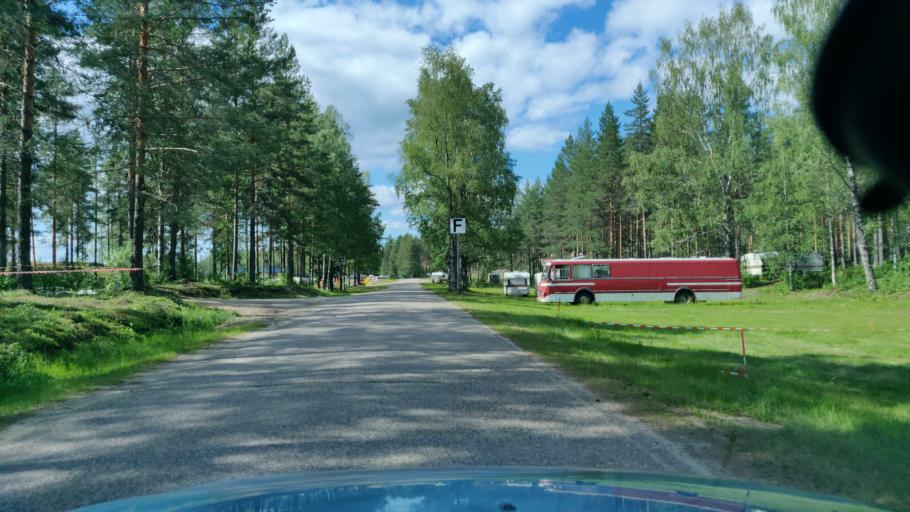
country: NO
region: Hedmark
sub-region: Trysil
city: Innbygda
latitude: 60.9167
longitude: 12.5589
